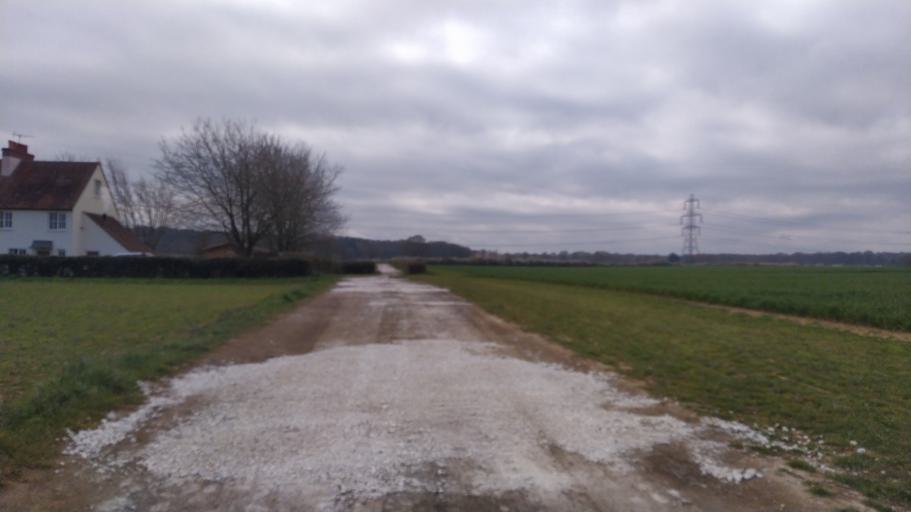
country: GB
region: England
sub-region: West Sussex
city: Petworth
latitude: 51.0184
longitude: -0.5772
